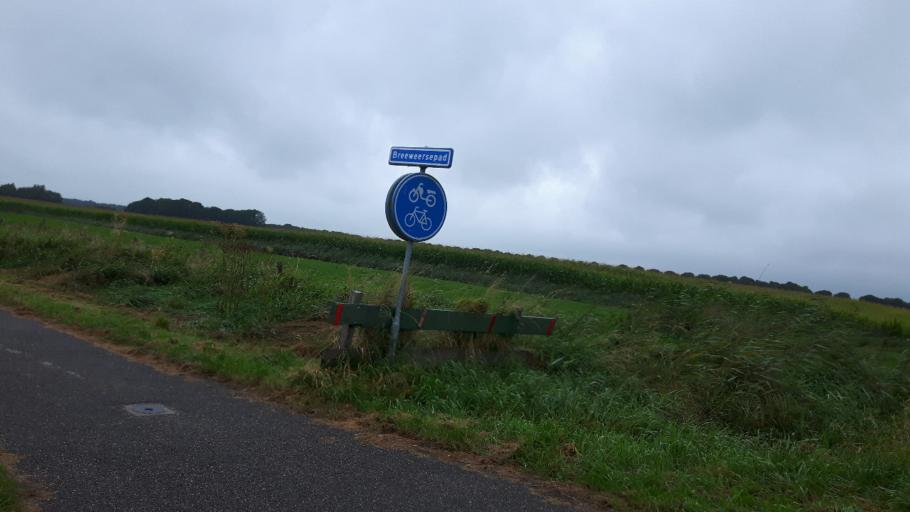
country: NL
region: Overijssel
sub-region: Gemeente Steenwijkerland
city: Oldemarkt
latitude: 52.8168
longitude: 5.9510
